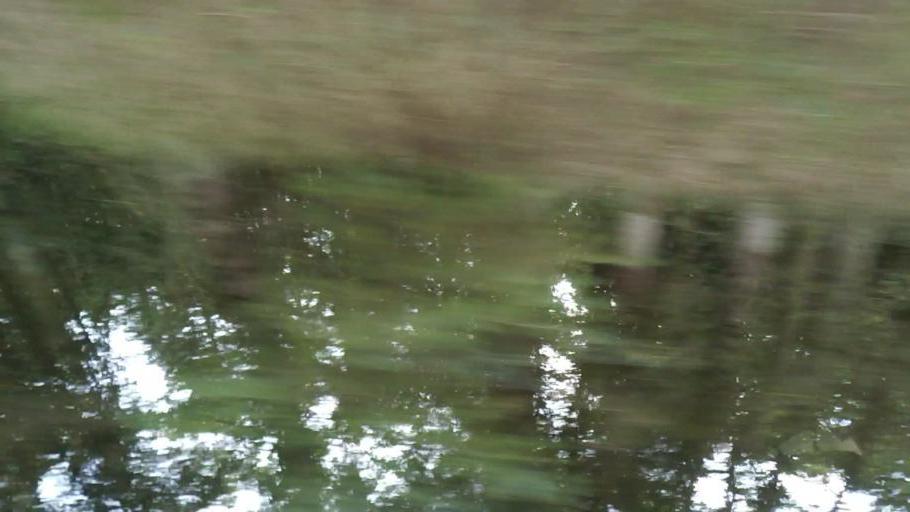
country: DK
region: Central Jutland
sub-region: Syddjurs Kommune
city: Ryomgard
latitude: 56.3928
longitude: 10.4832
